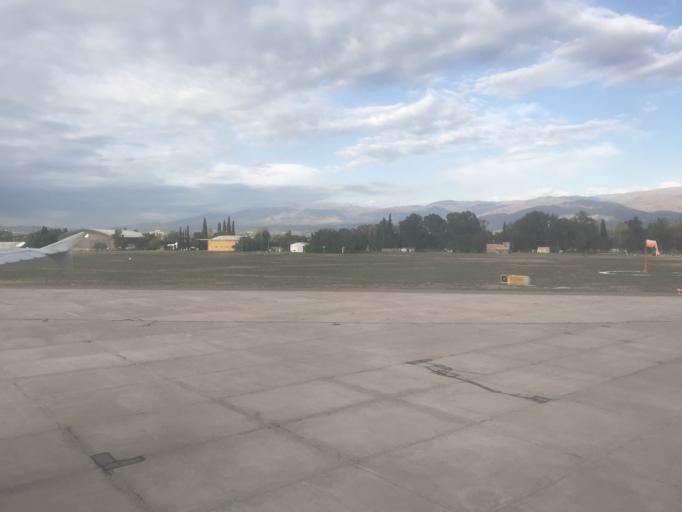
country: AR
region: Mendoza
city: Las Heras
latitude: -32.8427
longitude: -68.7940
